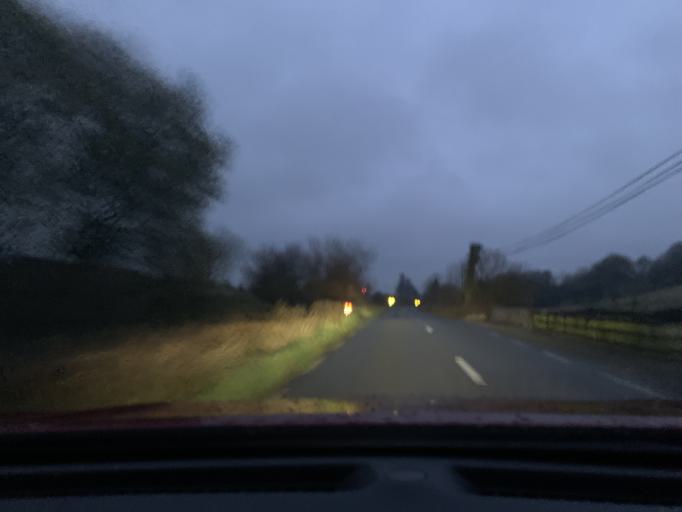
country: IE
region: Connaught
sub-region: Sligo
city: Ballymote
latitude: 54.0791
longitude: -8.5167
